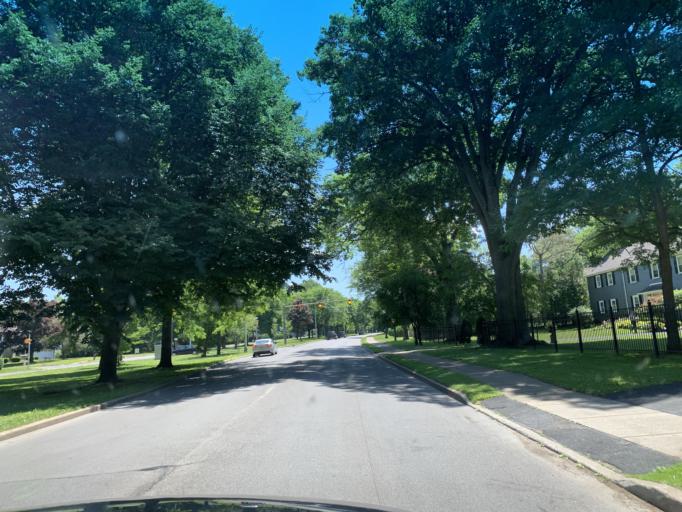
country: US
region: New York
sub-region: Oneida County
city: Utica
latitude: 43.0779
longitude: -75.2271
